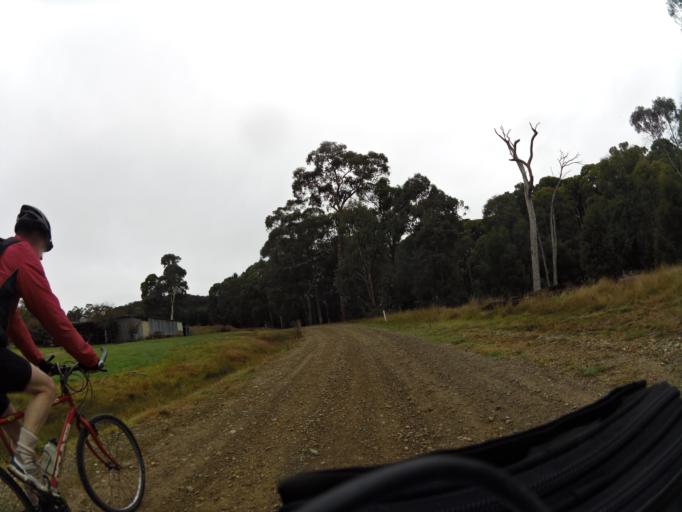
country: AU
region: New South Wales
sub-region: Greater Hume Shire
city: Holbrook
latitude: -36.1716
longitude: 147.4969
